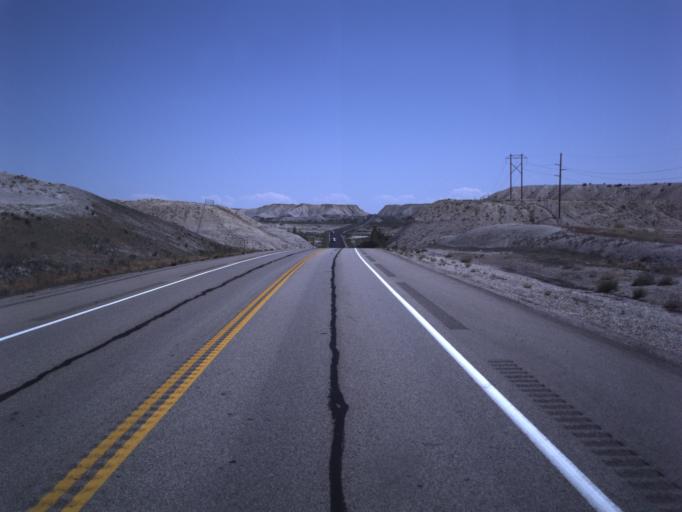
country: US
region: Utah
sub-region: Emery County
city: Ferron
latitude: 38.9506
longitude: -111.2096
